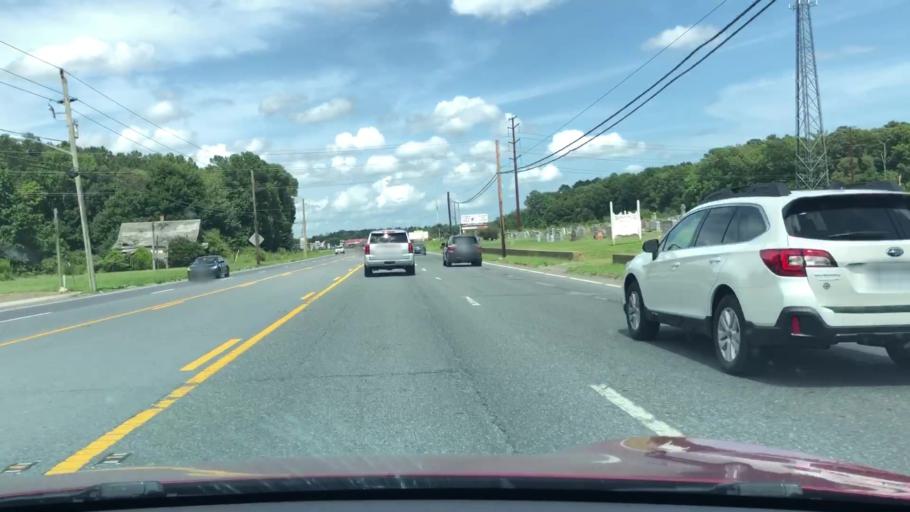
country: US
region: Virginia
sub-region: Accomack County
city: Wattsville
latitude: 37.9387
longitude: -75.5448
